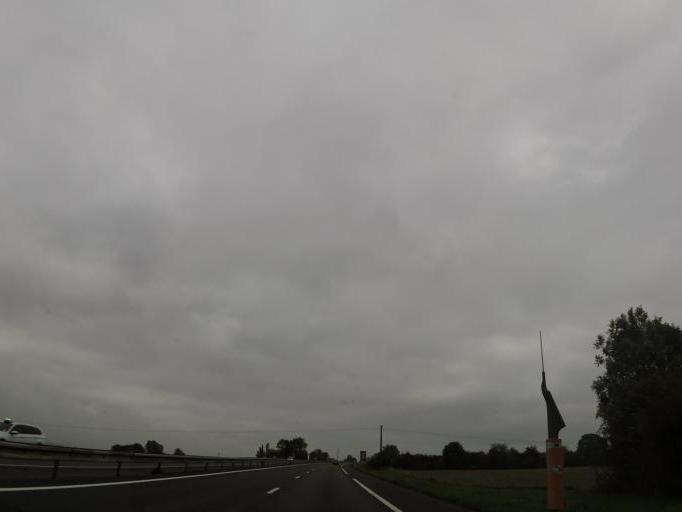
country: FR
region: Ile-de-France
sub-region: Departement de Seine-et-Marne
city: Sammeron
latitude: 48.9836
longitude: 3.0819
